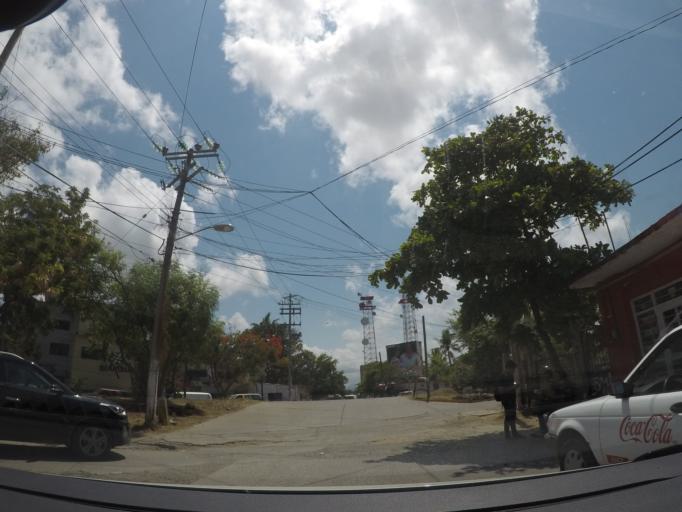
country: MX
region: Oaxaca
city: Juchitan de Zaragoza
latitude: 16.4421
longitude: -95.0194
